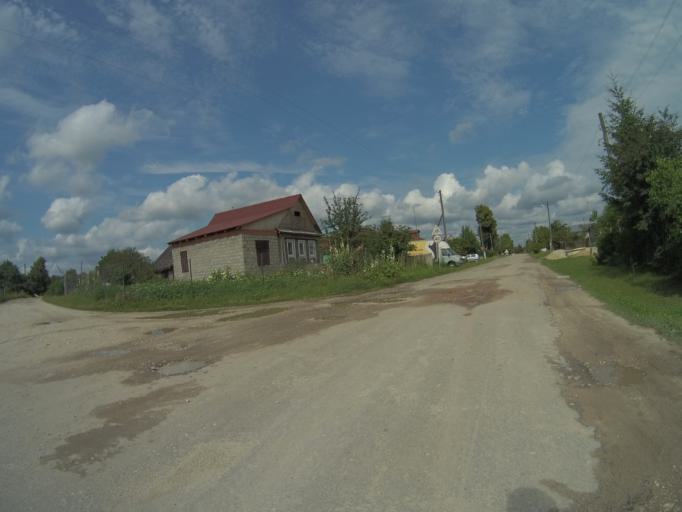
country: RU
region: Vladimir
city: Orgtrud
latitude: 56.2411
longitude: 40.6799
